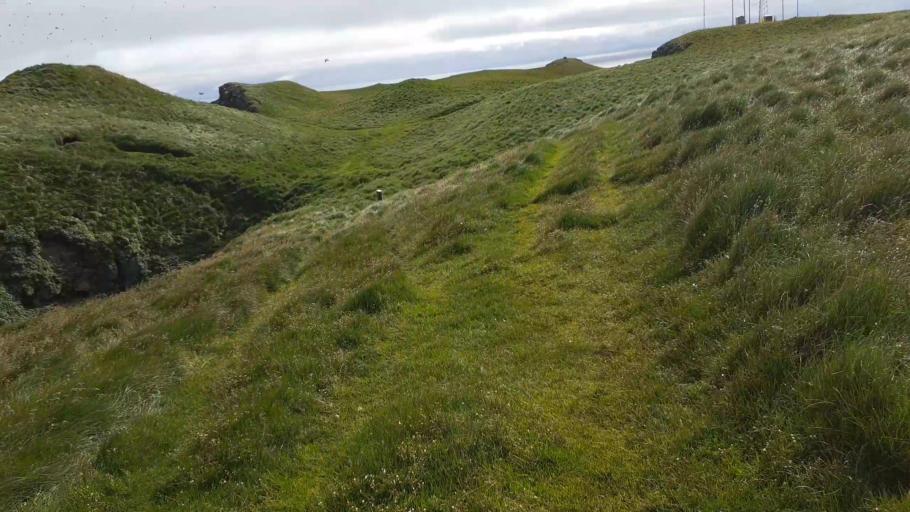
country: IS
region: Northeast
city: Dalvik
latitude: 66.5487
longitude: -17.9916
